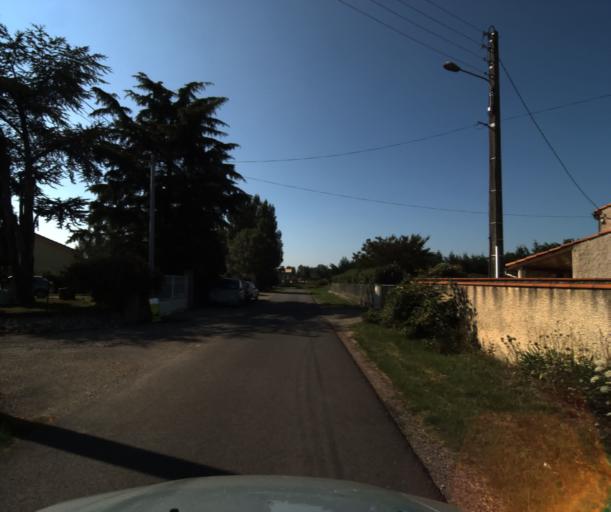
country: FR
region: Midi-Pyrenees
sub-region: Departement de la Haute-Garonne
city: Noe
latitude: 43.3649
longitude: 1.2713
